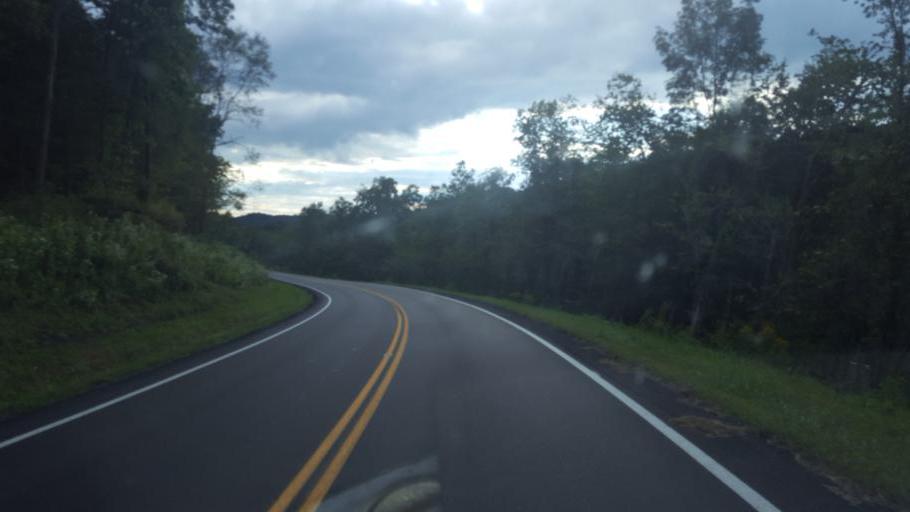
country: US
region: Ohio
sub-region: Knox County
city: Oak Hill
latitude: 40.4663
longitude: -82.1518
